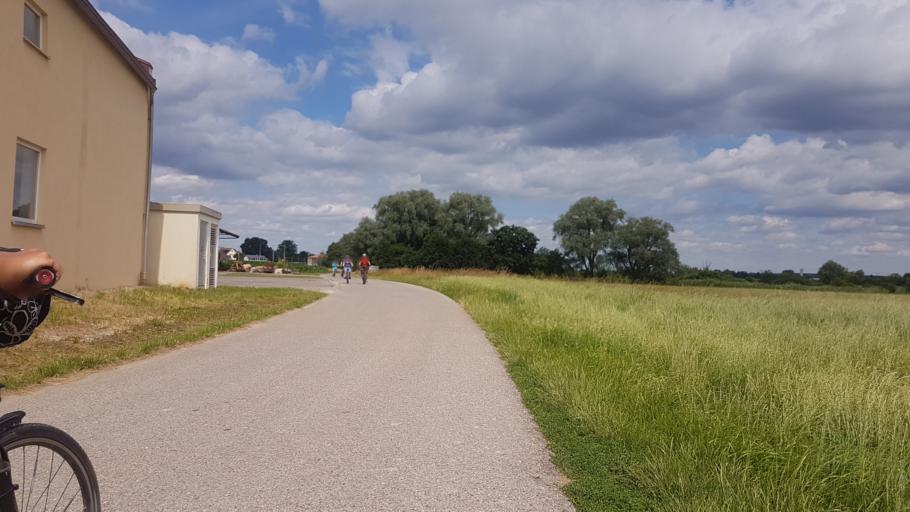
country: DE
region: Bavaria
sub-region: Regierungsbezirk Mittelfranken
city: Gunzenhausen
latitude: 49.0912
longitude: 10.7609
